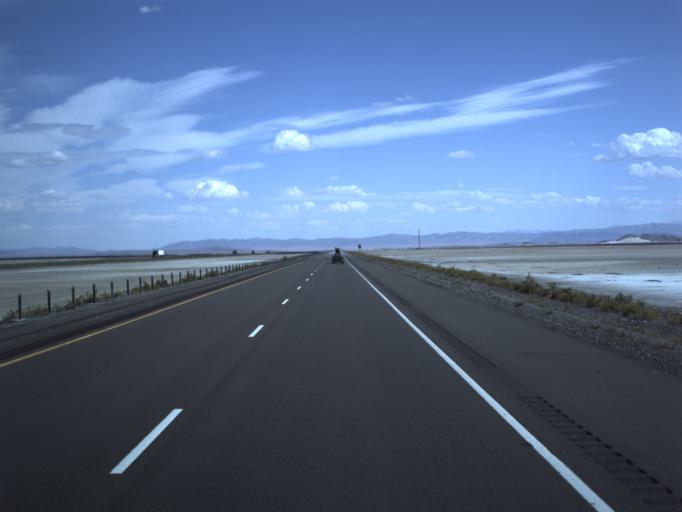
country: US
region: Utah
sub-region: Tooele County
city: Wendover
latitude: 40.7280
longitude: -113.3730
